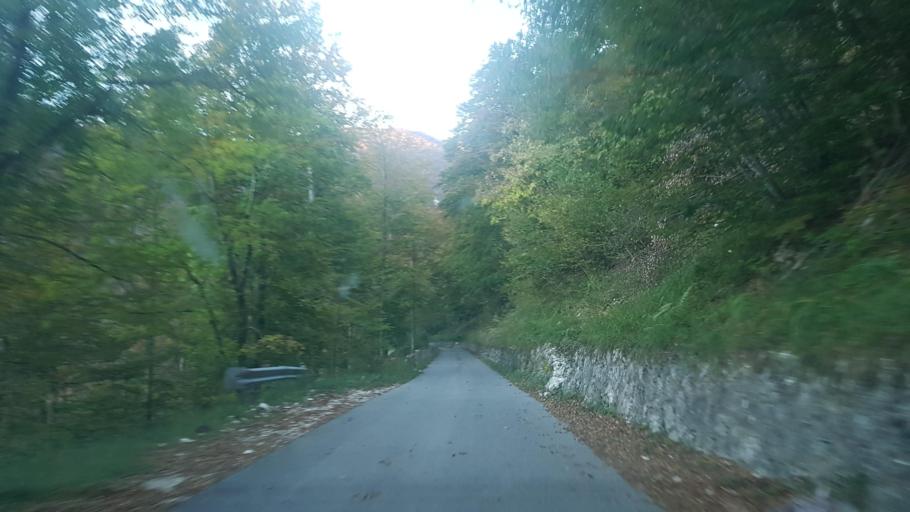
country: IT
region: Friuli Venezia Giulia
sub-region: Provincia di Udine
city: Preone
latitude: 46.3448
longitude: 12.8925
